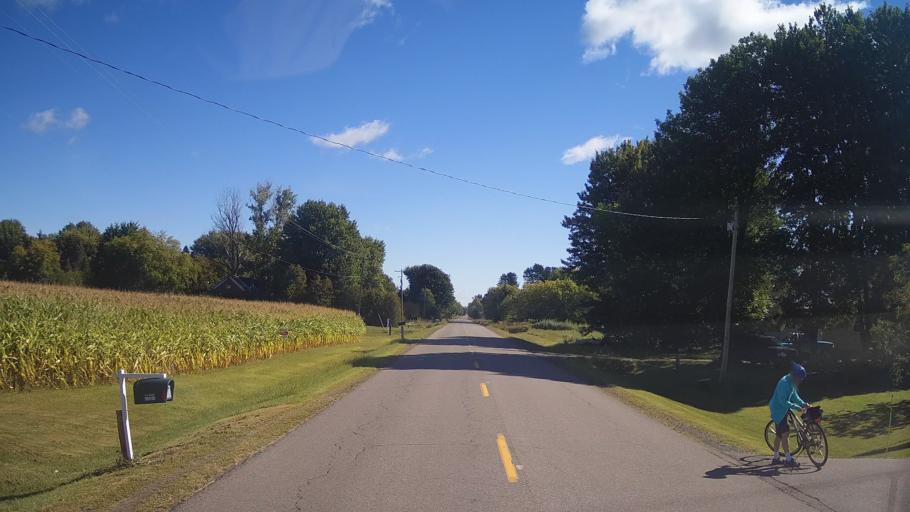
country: CA
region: Ontario
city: Prescott
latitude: 44.9046
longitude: -75.3920
